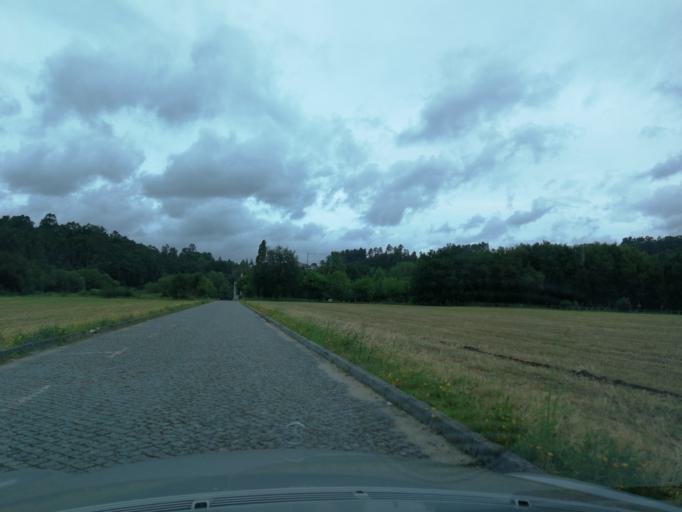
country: PT
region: Braga
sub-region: Braga
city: Adaufe
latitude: 41.6074
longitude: -8.4067
